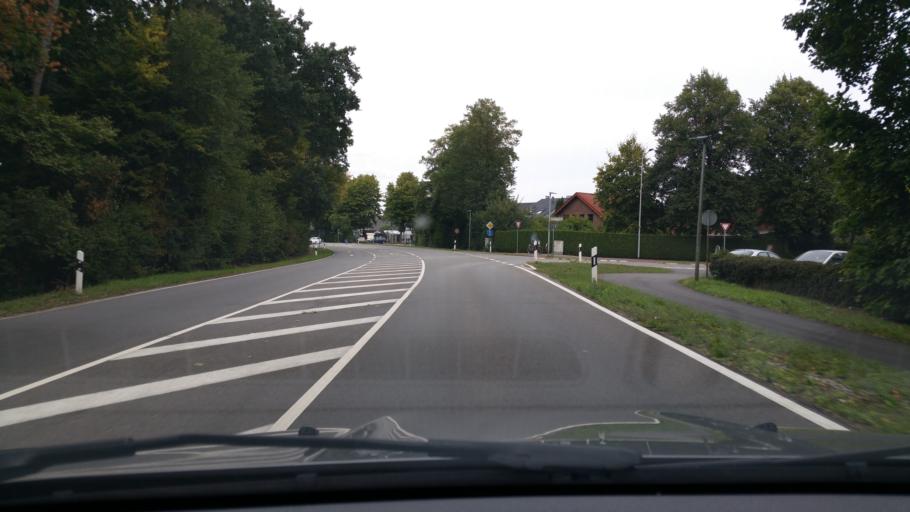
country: DE
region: North Rhine-Westphalia
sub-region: Regierungsbezirk Dusseldorf
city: Bocholt
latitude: 51.8571
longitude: 6.6221
